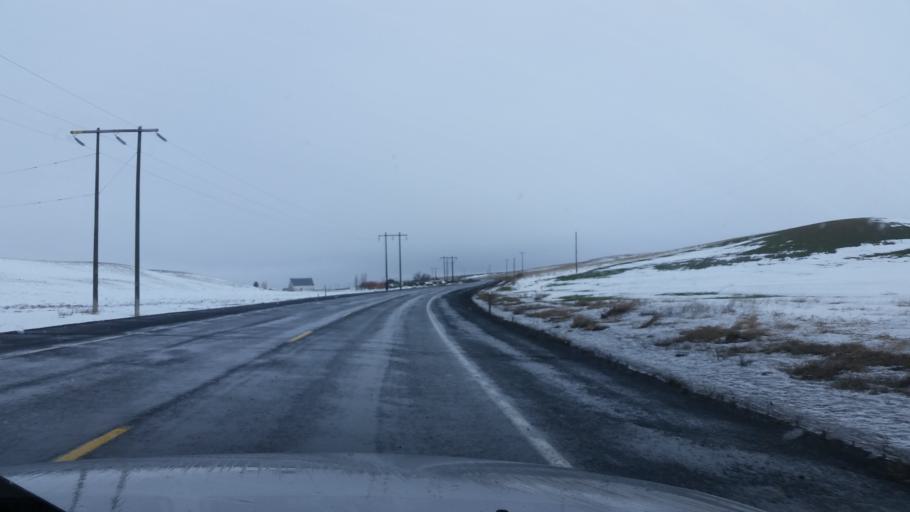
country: US
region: Washington
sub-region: Lincoln County
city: Davenport
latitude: 47.5466
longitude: -118.1885
